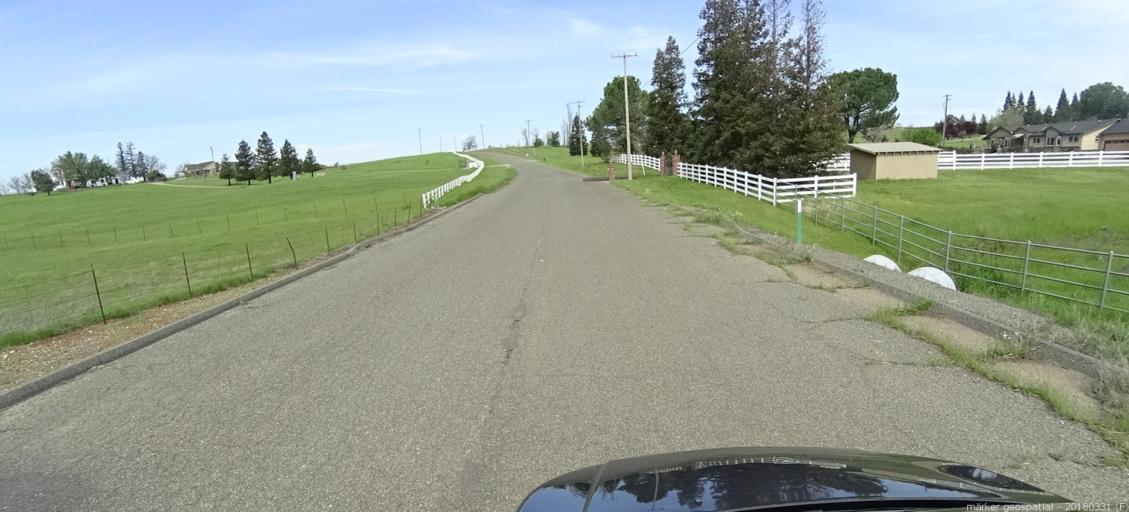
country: US
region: California
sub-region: Sacramento County
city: Rancho Murieta
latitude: 38.5038
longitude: -121.1353
